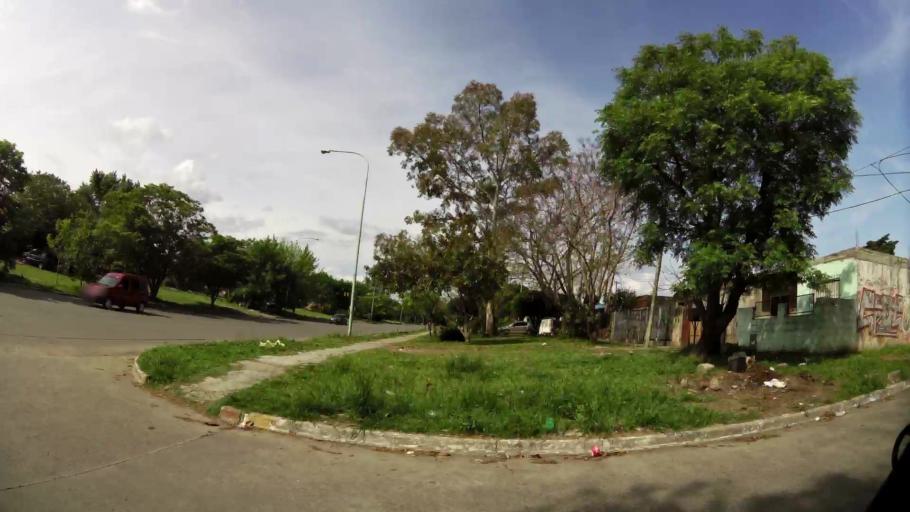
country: AR
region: Buenos Aires
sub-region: Partido de Quilmes
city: Quilmes
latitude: -34.7730
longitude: -58.2388
